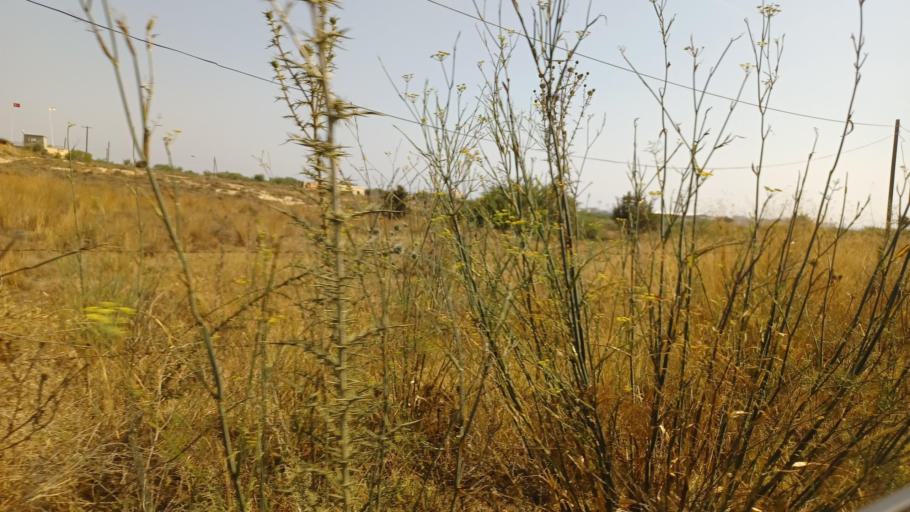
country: CY
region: Ammochostos
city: Deryneia
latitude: 35.0719
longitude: 33.9567
